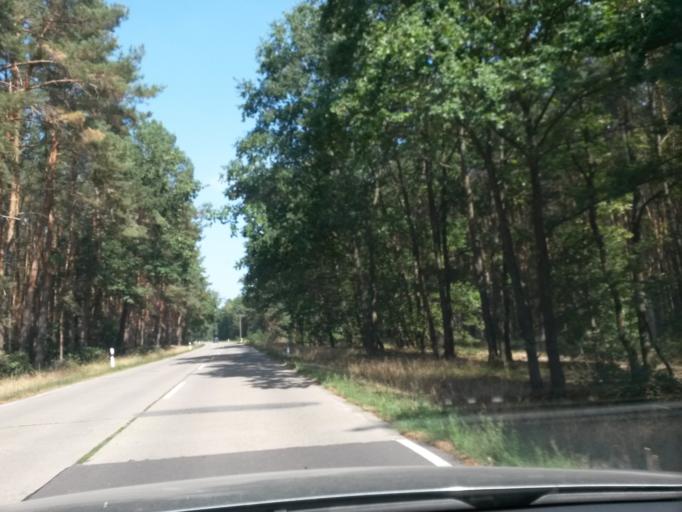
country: DE
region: Saxony-Anhalt
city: Jerichow
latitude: 52.4751
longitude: 12.0275
